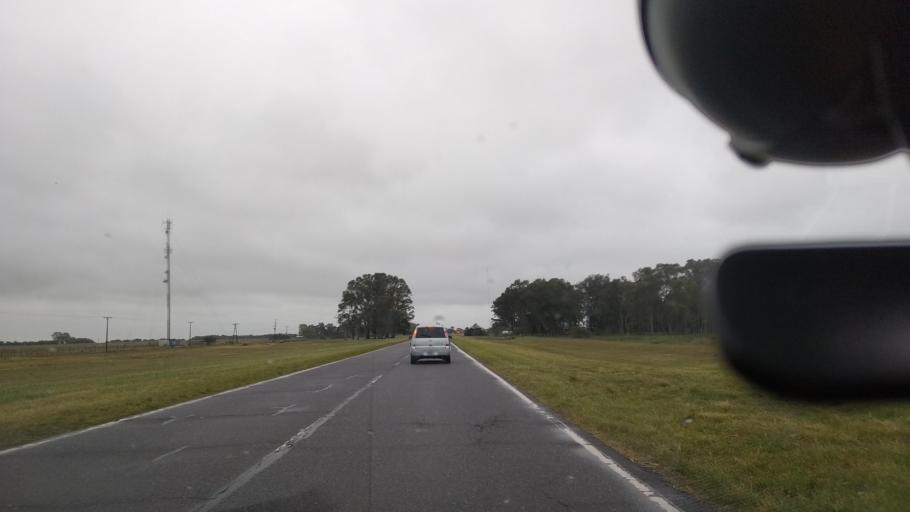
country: AR
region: Buenos Aires
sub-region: Partido de Castelli
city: Castelli
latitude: -35.9859
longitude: -57.4498
